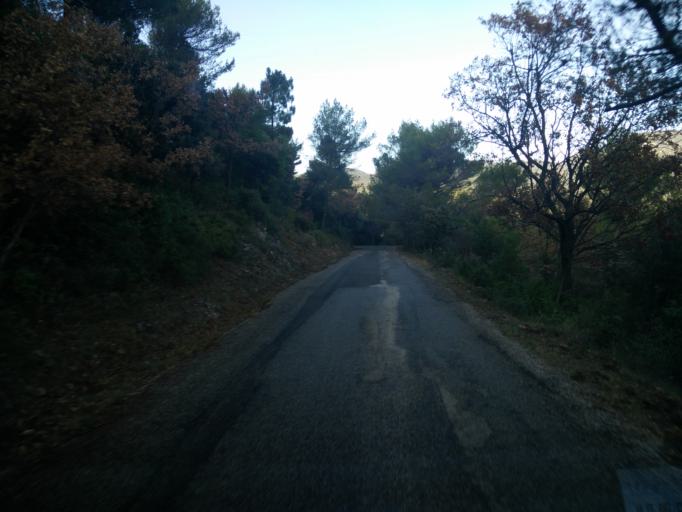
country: FR
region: Provence-Alpes-Cote d'Azur
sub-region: Departement du Var
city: Signes
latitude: 43.2747
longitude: 5.8474
